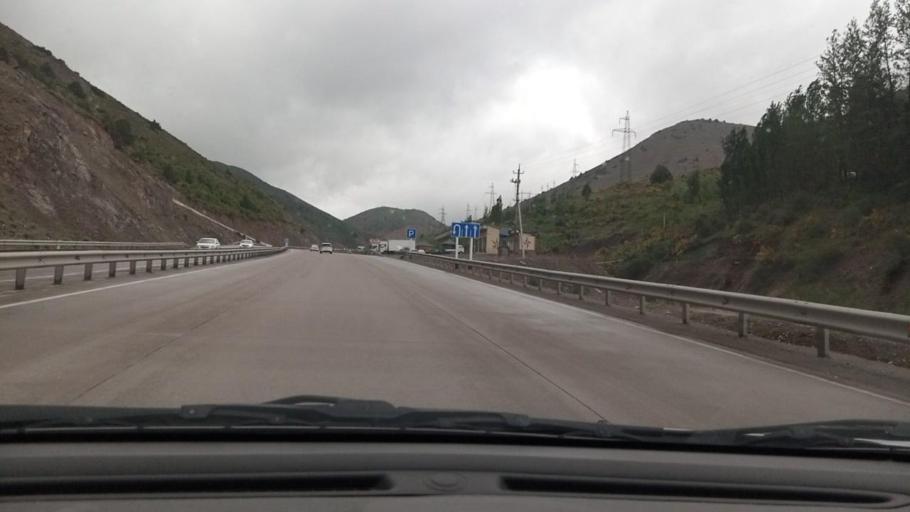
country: UZ
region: Toshkent
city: Angren
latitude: 41.0493
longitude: 70.5695
